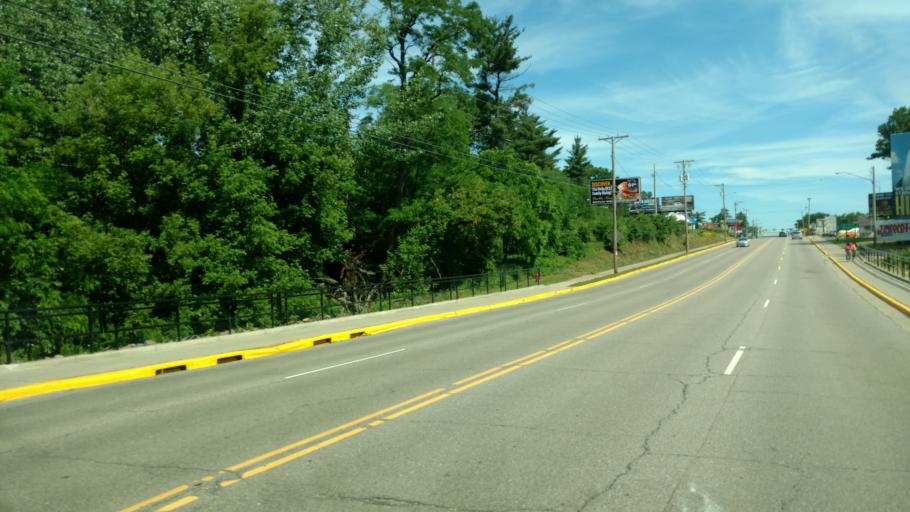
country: US
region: Wisconsin
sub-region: Sauk County
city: Lake Delton
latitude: 43.5920
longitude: -89.7938
